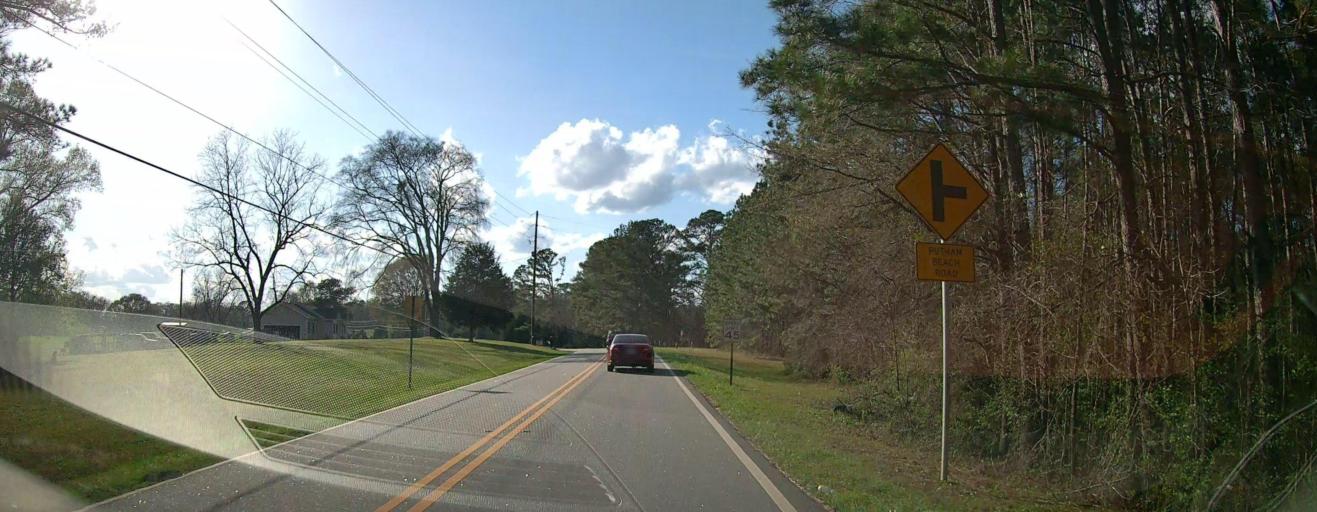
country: US
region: Georgia
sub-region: Putnam County
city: Eatonton
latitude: 33.1973
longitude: -83.4000
